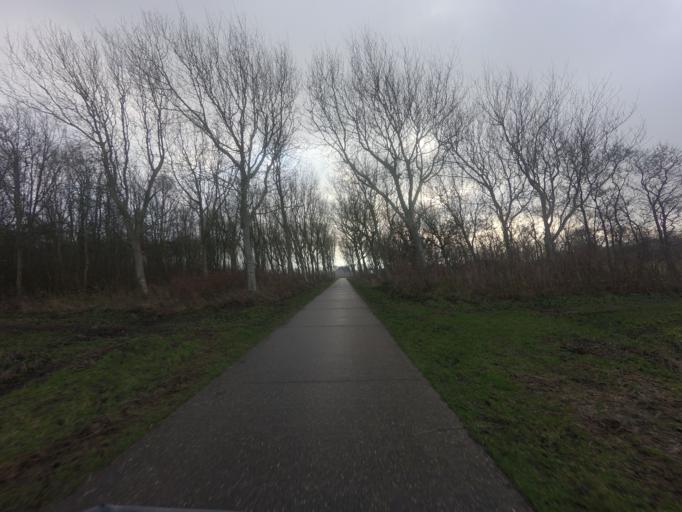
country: NL
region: North Holland
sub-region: Gemeente Texel
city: Den Burg
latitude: 53.1599
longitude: 4.8526
